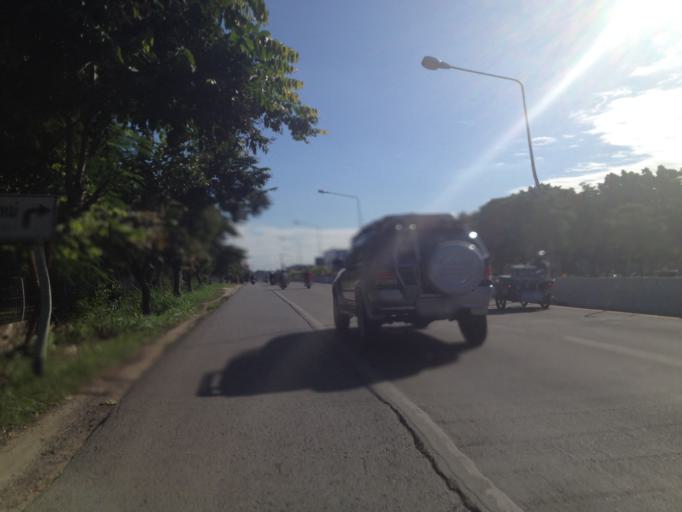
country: TH
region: Chiang Mai
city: Chiang Mai
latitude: 18.7934
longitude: 98.9618
